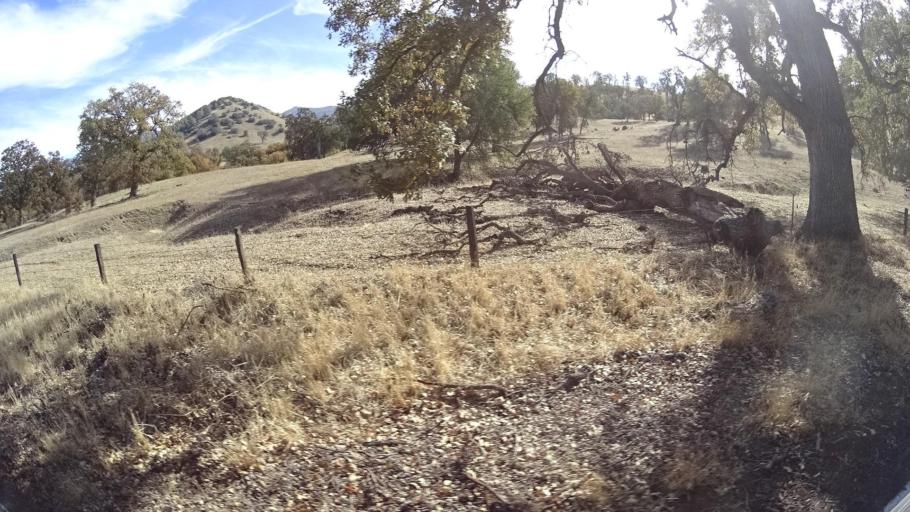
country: US
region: California
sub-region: Kern County
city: Alta Sierra
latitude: 35.6702
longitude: -118.7429
